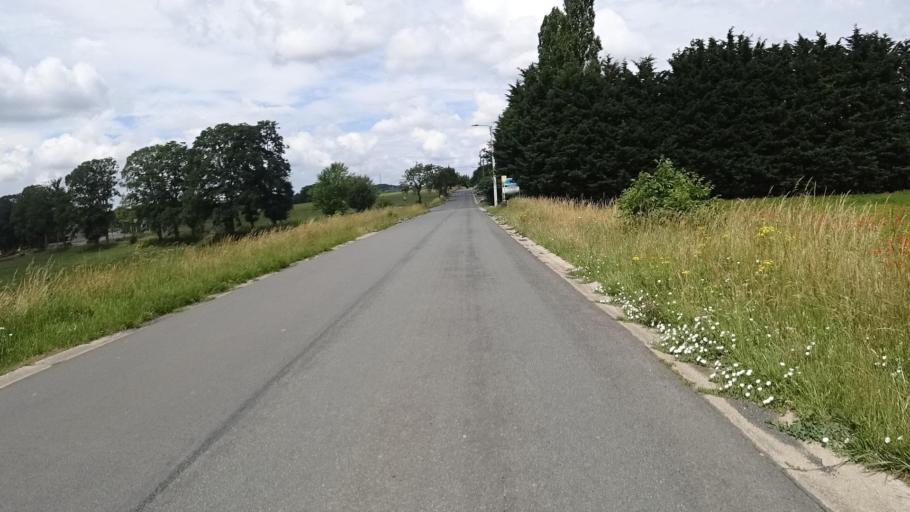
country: BE
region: Wallonia
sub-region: Province de Namur
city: Namur
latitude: 50.4954
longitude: 4.8719
